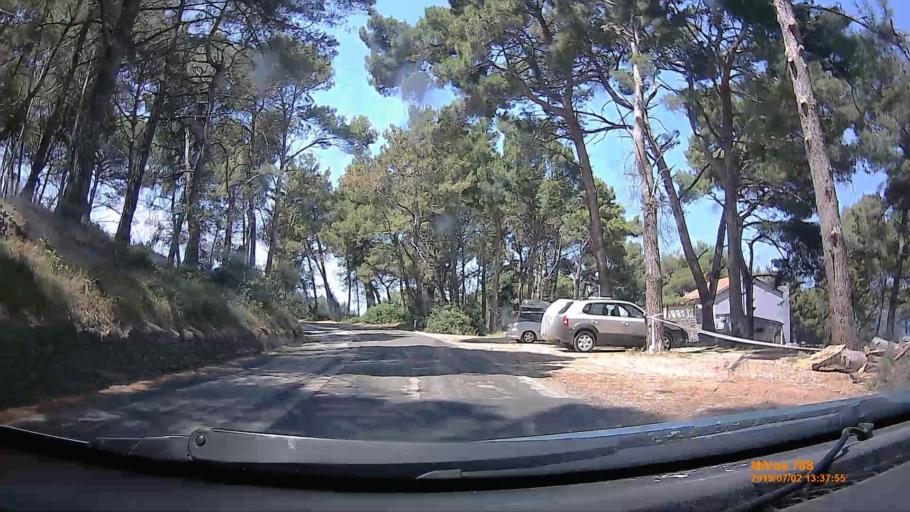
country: HR
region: Primorsko-Goranska
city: Mali Losinj
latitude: 44.5263
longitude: 14.4887
